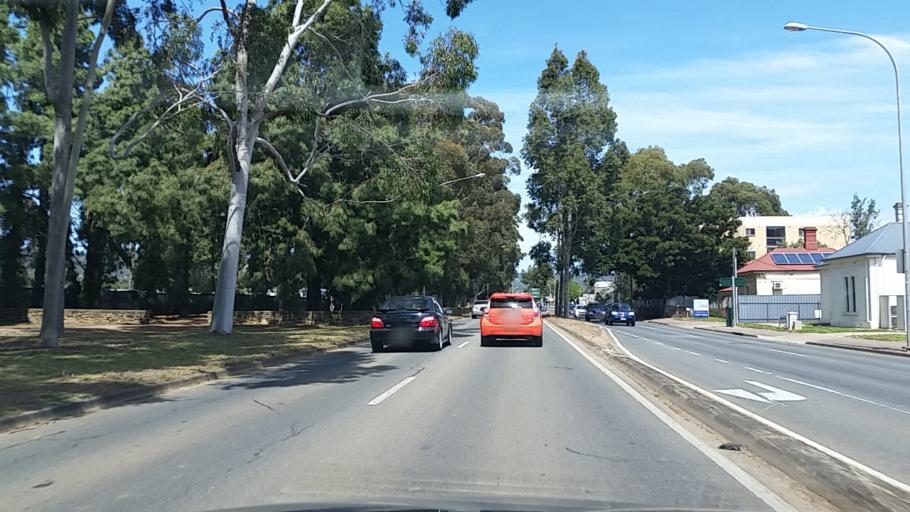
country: AU
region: South Australia
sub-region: Unley
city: Fullarton
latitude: -34.9434
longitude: 138.6249
